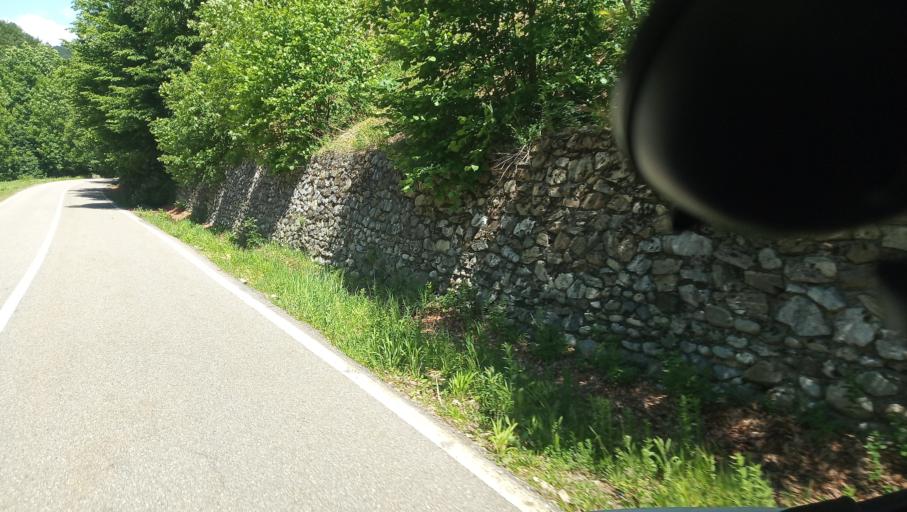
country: RO
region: Mehedinti
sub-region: Comuna Isverna
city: Isverna
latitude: 45.0365
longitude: 22.6199
